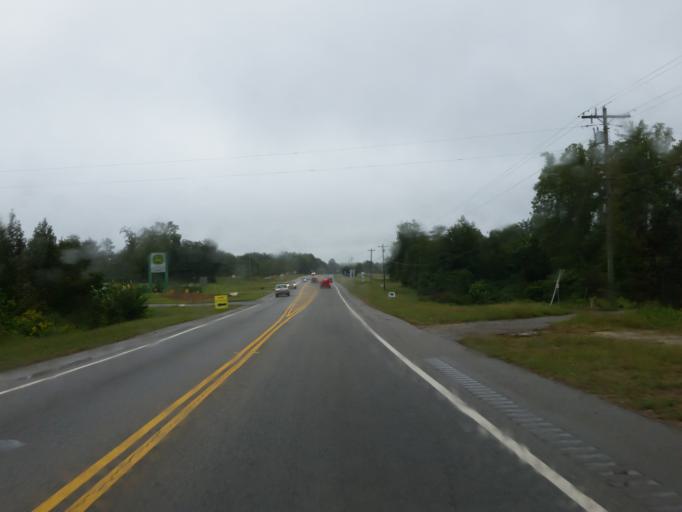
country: US
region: Georgia
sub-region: Lamar County
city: Barnesville
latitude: 33.0323
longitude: -84.1475
